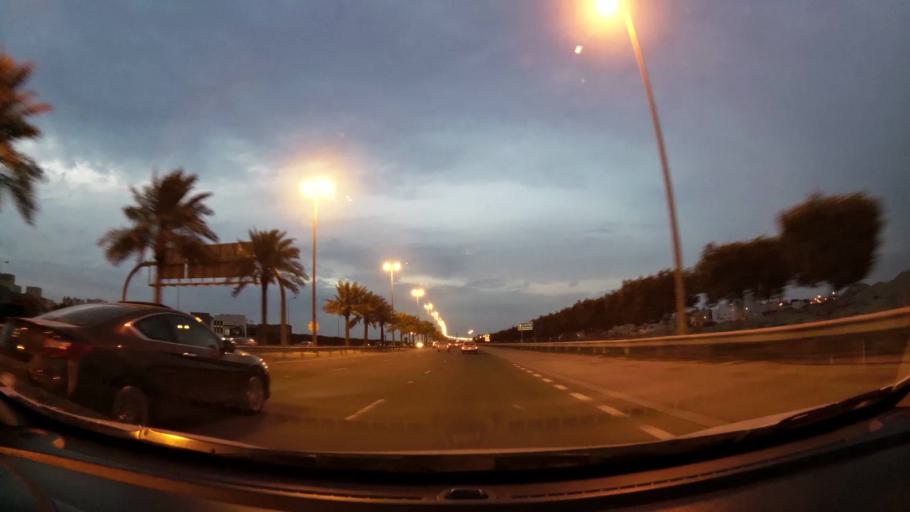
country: BH
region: Central Governorate
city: Madinat Hamad
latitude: 26.1498
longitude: 50.5087
